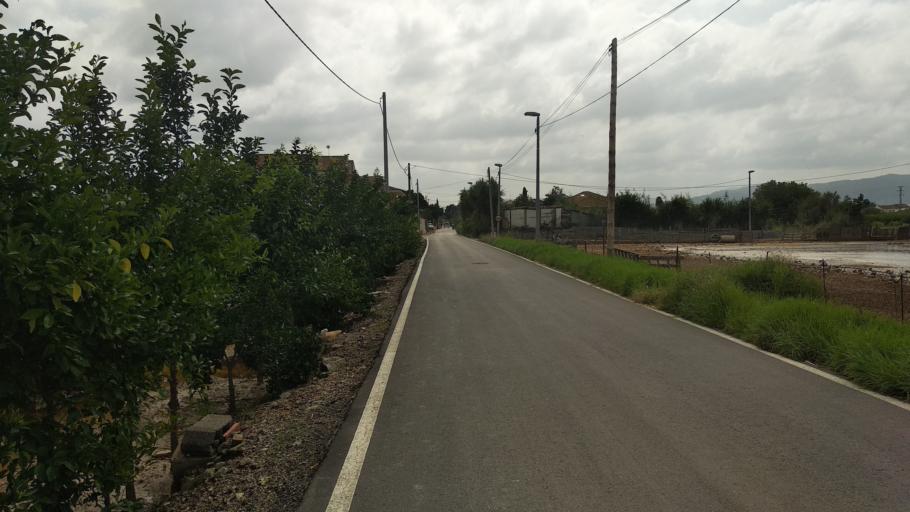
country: ES
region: Murcia
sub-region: Murcia
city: Santomera
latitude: 38.0417
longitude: -1.0347
